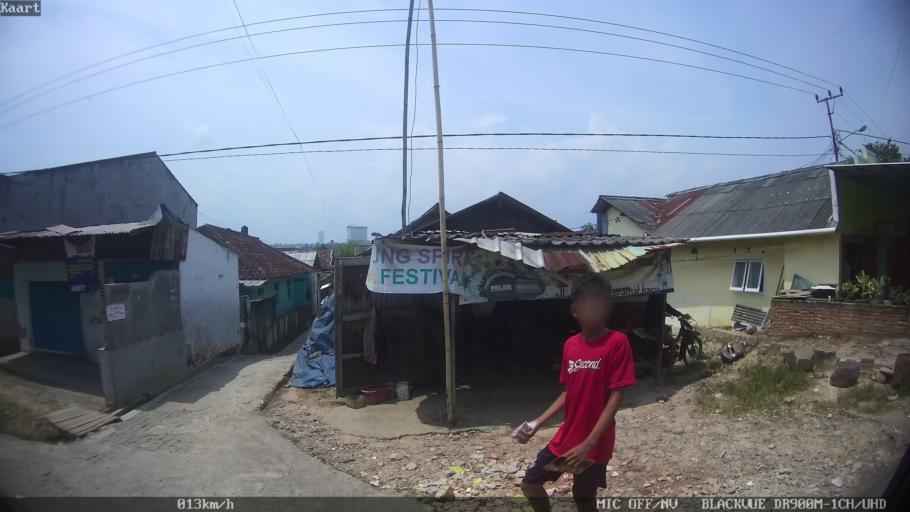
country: ID
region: Lampung
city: Bandarlampung
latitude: -5.4523
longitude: 105.2519
